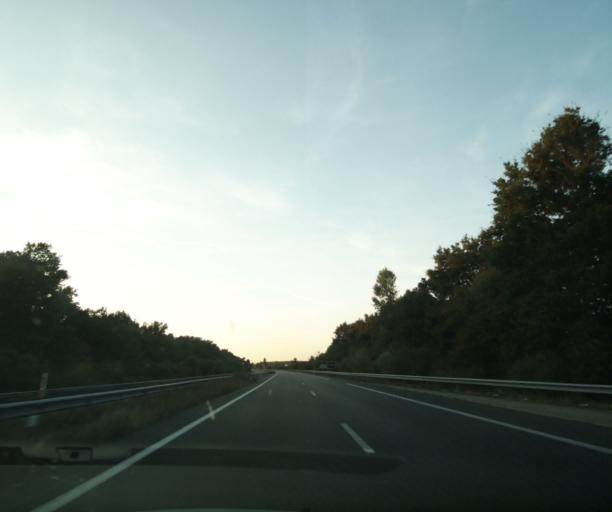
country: FR
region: Aquitaine
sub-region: Departement du Lot-et-Garonne
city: Fourques-sur-Garonne
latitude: 44.4186
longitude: 0.1737
